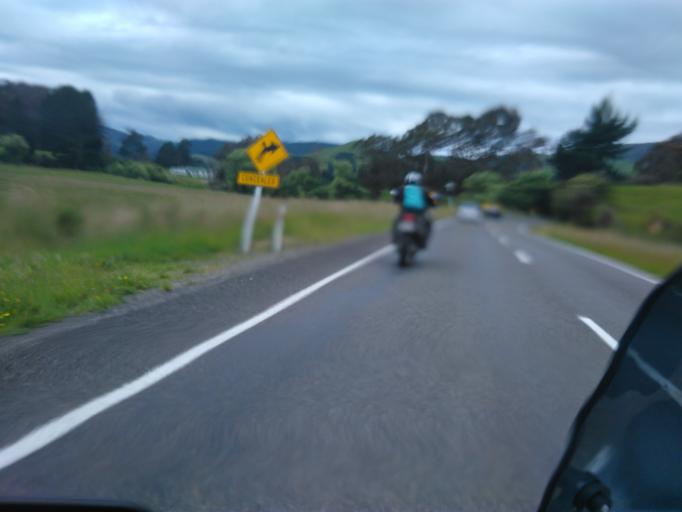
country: NZ
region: Bay of Plenty
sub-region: Opotiki District
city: Opotiki
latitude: -38.3596
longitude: 177.5270
